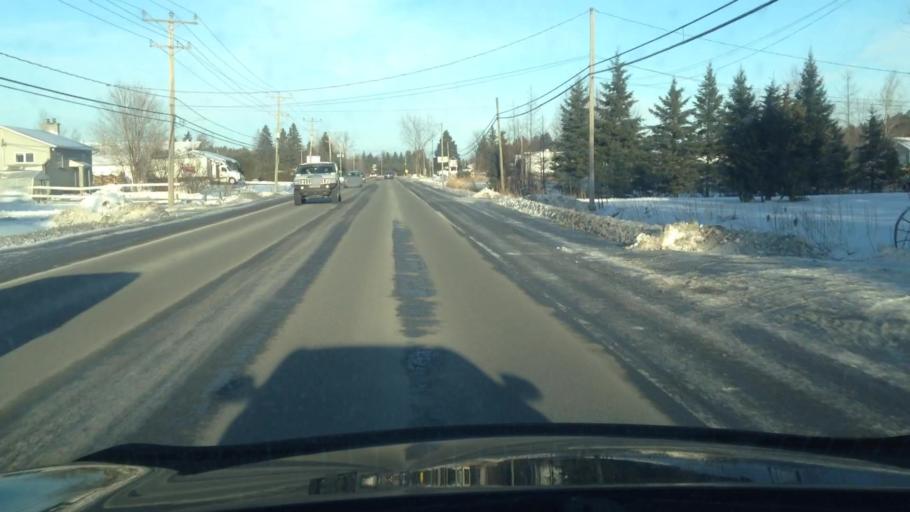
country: CA
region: Quebec
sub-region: Laurentides
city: Sainte-Sophie
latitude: 45.8065
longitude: -73.9276
